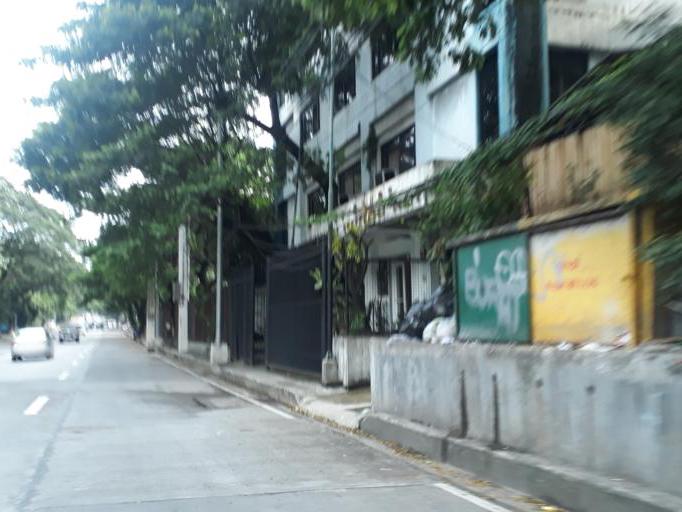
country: PH
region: Metro Manila
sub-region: Quezon City
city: Quezon City
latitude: 14.6520
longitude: 121.0591
